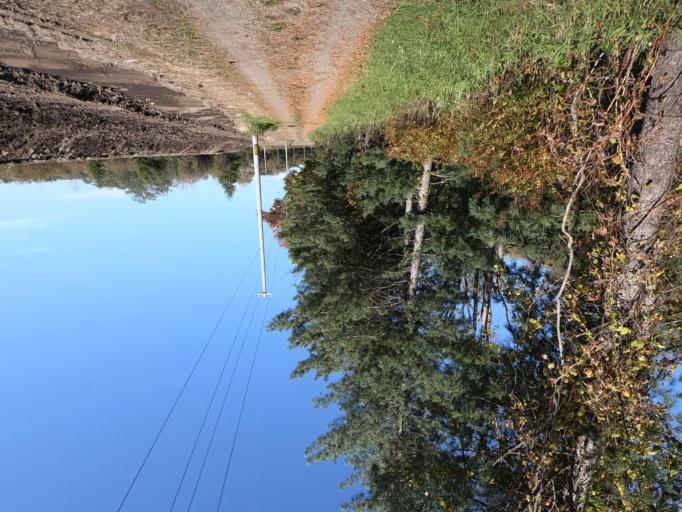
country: JP
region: Hokkaido
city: Otofuke
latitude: 43.2341
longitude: 143.2636
